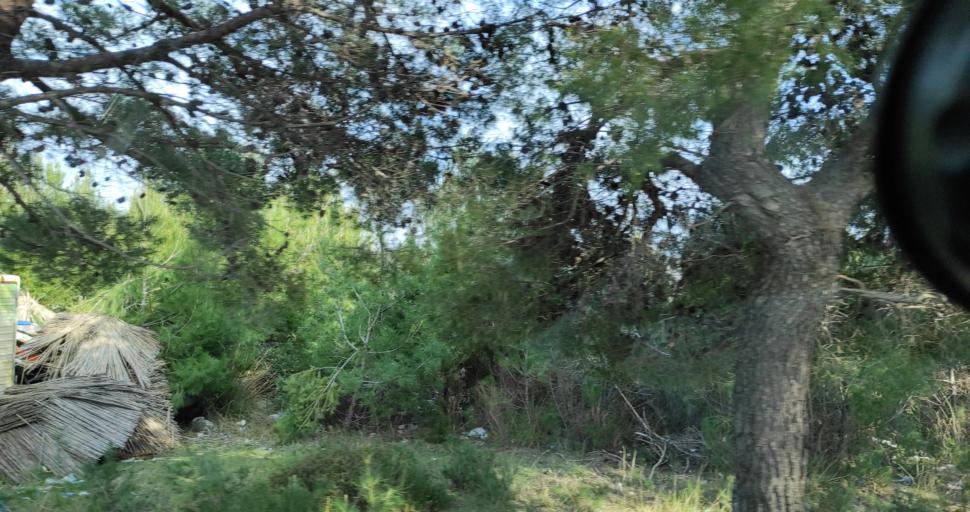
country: AL
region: Lezhe
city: Shengjin
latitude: 41.7889
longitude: 19.6031
